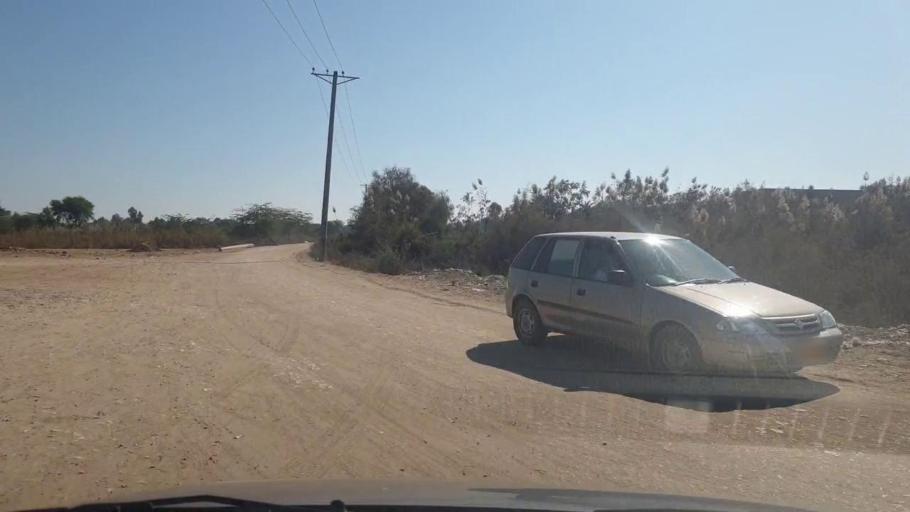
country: PK
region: Sindh
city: Bozdar
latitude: 27.0747
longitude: 68.6153
